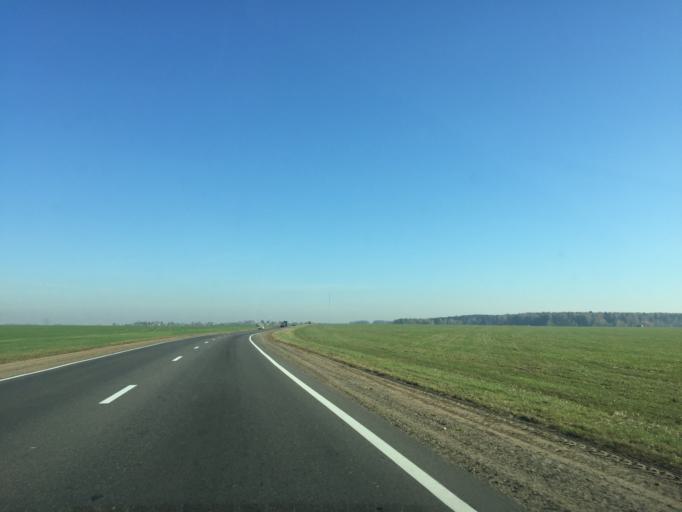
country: BY
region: Mogilev
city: Mahilyow
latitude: 53.9640
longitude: 30.2479
